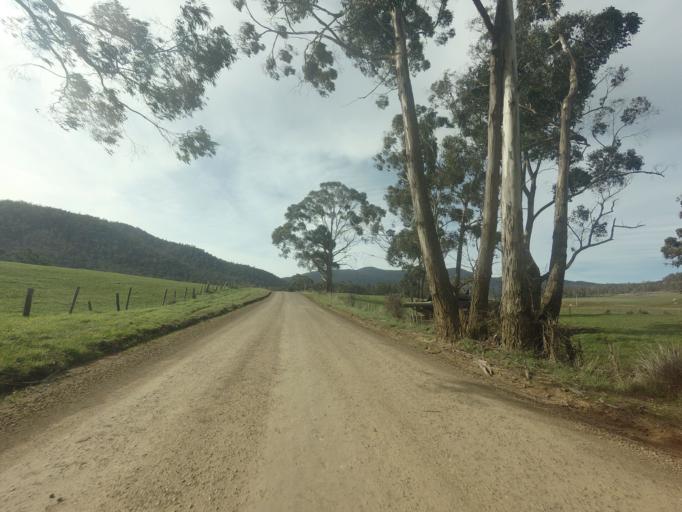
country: AU
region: Tasmania
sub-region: Huon Valley
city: Franklin
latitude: -43.0728
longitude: 147.0452
